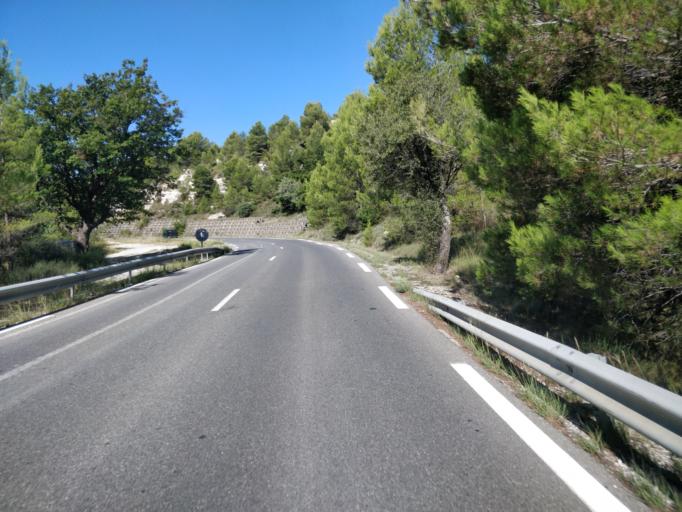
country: FR
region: Provence-Alpes-Cote d'Azur
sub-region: Departement des Alpes-de-Haute-Provence
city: Riez
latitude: 43.8043
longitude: 6.2386
